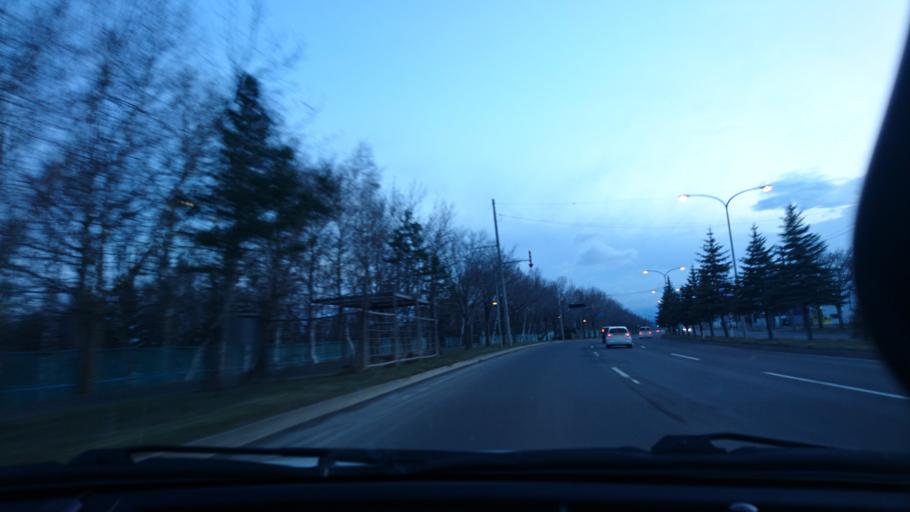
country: JP
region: Hokkaido
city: Sapporo
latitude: 43.1203
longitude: 141.4116
